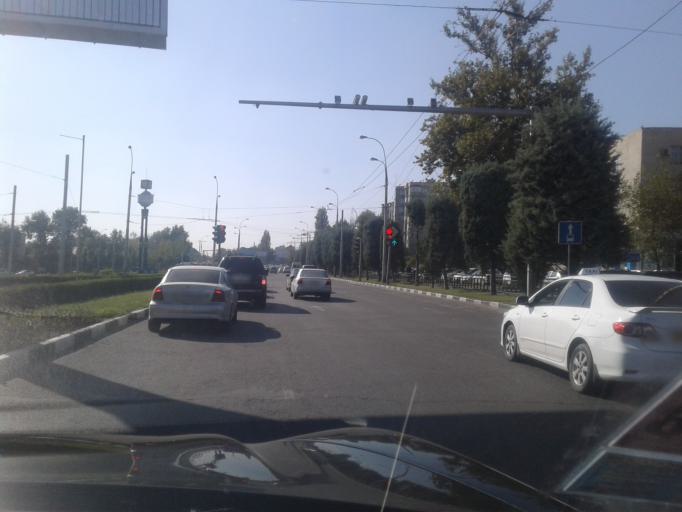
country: TJ
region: Dushanbe
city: Dushanbe
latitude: 38.5587
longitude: 68.7633
